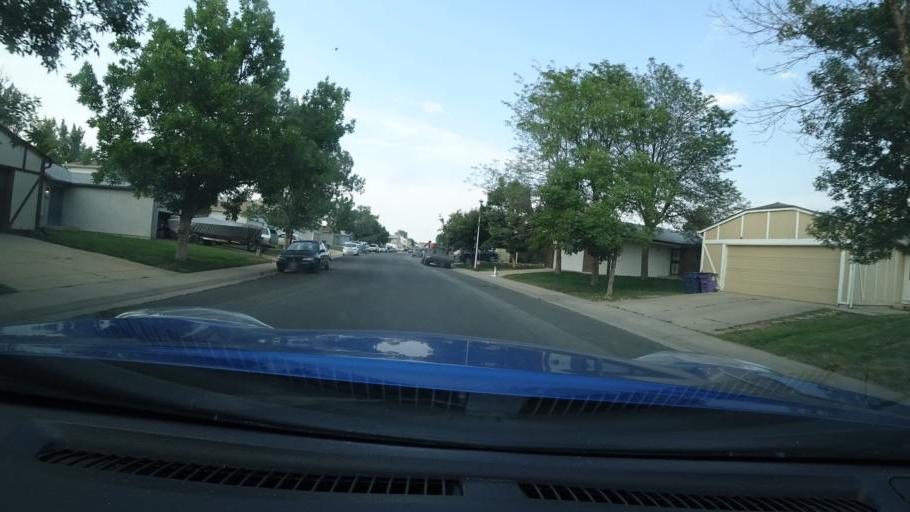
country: US
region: Colorado
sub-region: Adams County
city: Aurora
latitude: 39.7425
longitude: -104.7613
